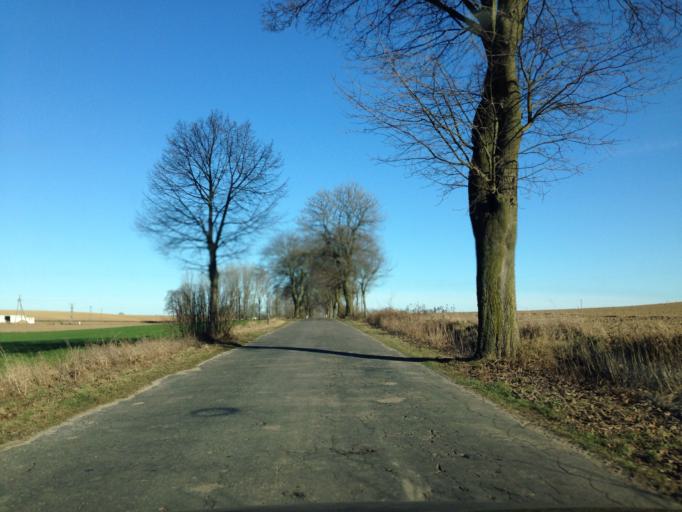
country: PL
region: Warmian-Masurian Voivodeship
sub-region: Powiat nowomiejski
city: Kurzetnik
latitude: 53.3829
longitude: 19.6221
